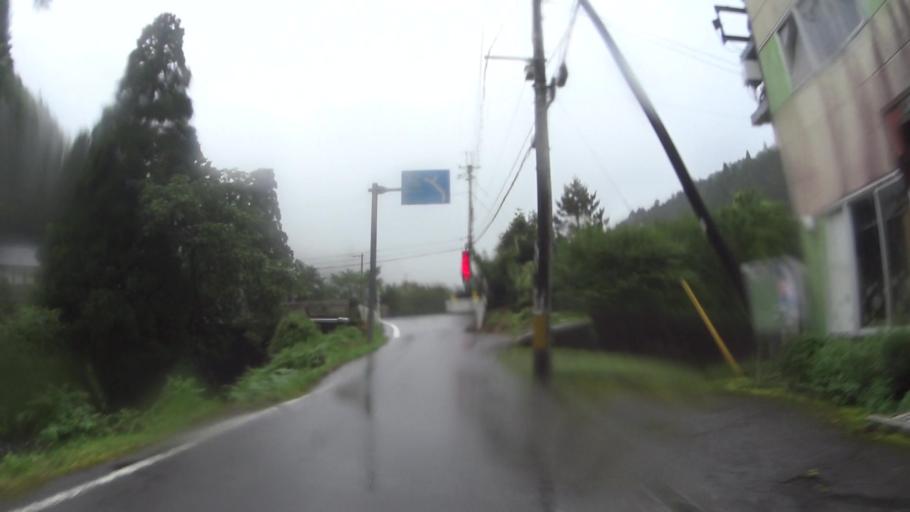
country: JP
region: Shiga Prefecture
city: Kitahama
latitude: 35.2651
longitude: 135.8199
